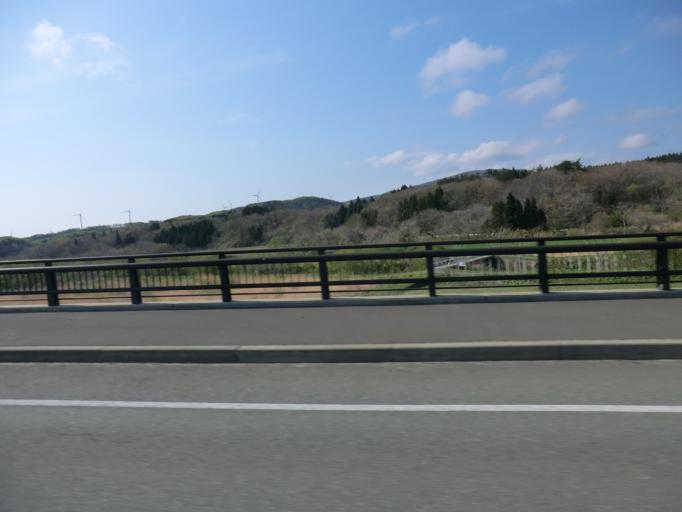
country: JP
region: Aomori
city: Misawa
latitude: 40.9817
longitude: 141.3625
